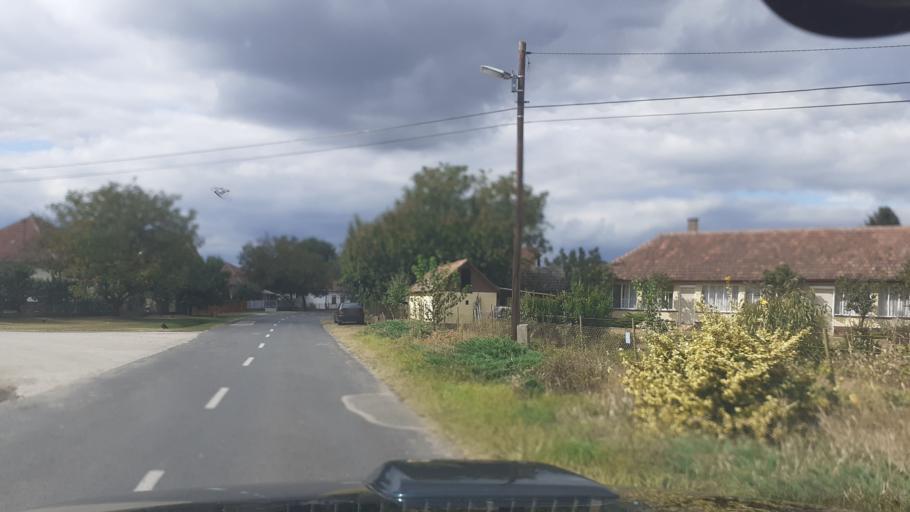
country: HU
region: Bacs-Kiskun
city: Solt
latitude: 46.8129
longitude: 18.9802
